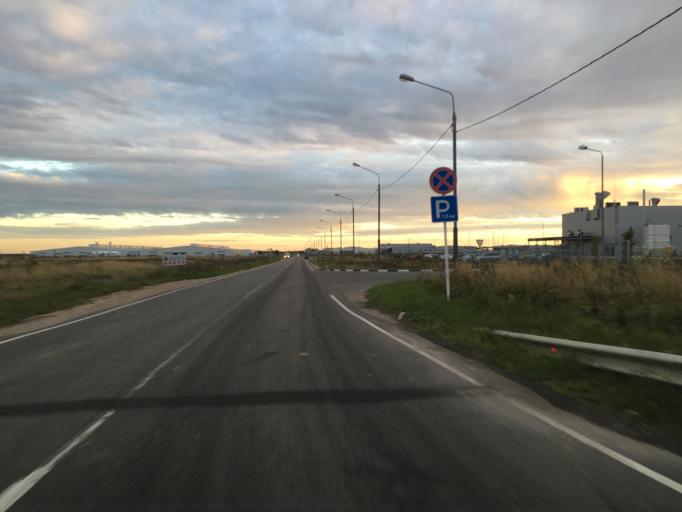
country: RU
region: Kaluga
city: Kaluga
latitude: 54.5801
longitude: 36.3486
